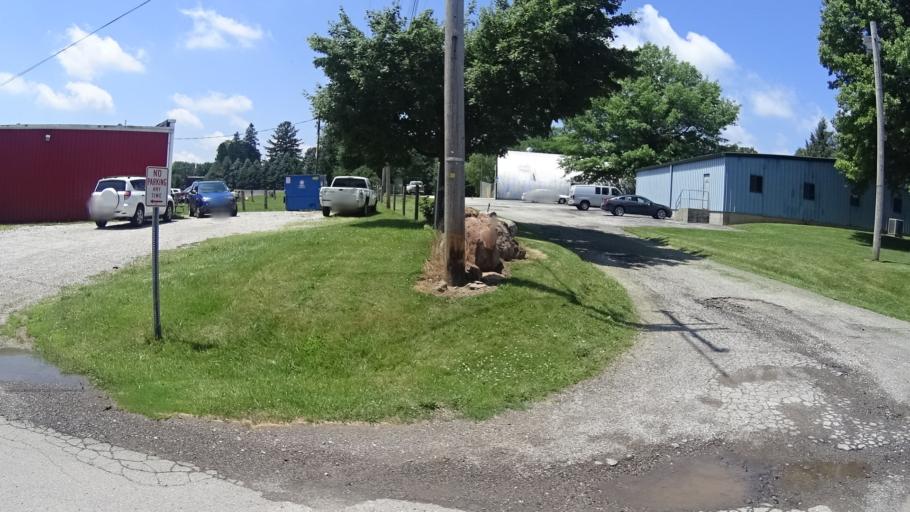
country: US
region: Ohio
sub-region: Huron County
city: Wakeman
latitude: 41.3309
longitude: -82.3606
